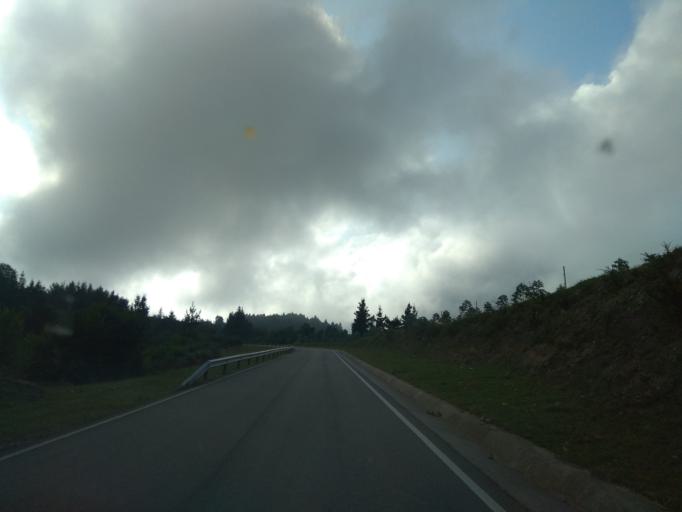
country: ES
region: Cantabria
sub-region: Provincia de Cantabria
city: San Vicente de la Barquera
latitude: 43.3079
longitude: -4.4052
